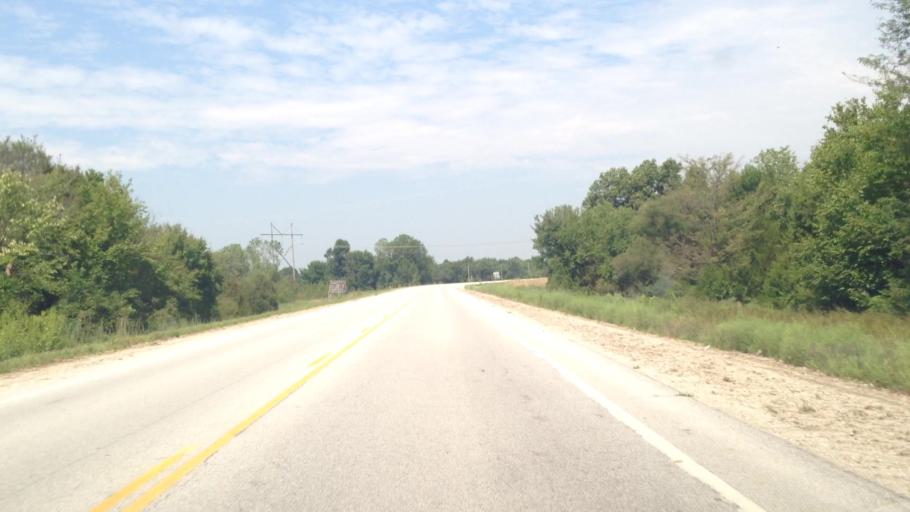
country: US
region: Kansas
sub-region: Labette County
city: Parsons
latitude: 37.3880
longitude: -95.2671
